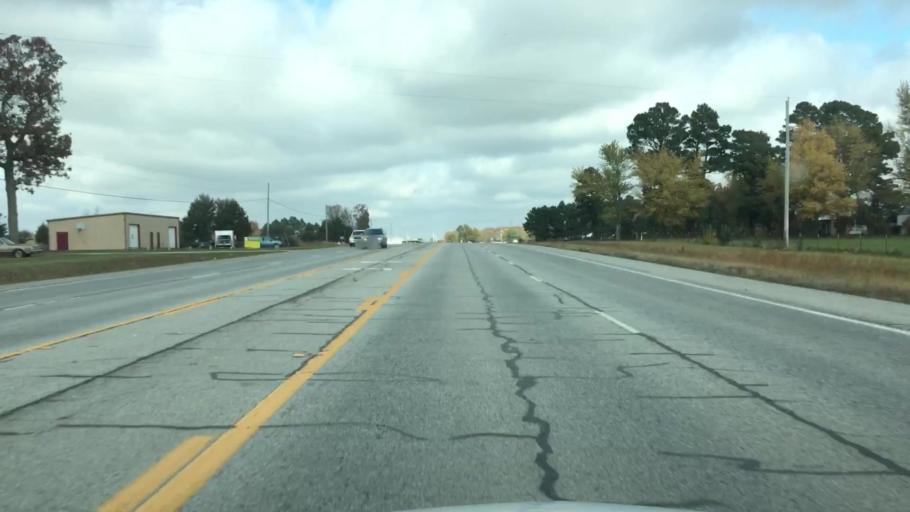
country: US
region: Arkansas
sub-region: Benton County
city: Gentry
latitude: 36.2248
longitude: -94.4952
